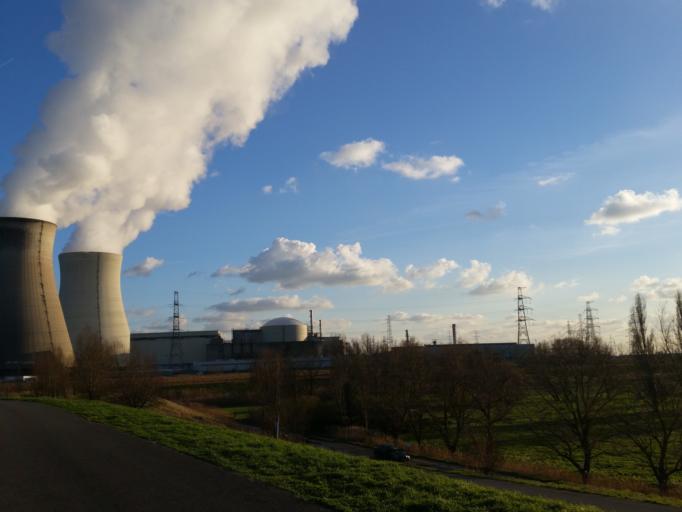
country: NL
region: North Brabant
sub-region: Gemeente Woensdrecht
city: Woensdrecht
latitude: 51.3325
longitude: 4.2529
